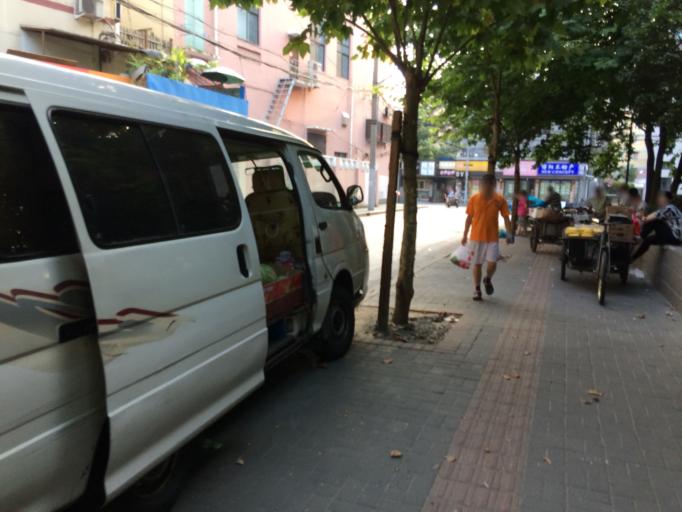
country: CN
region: Shanghai Shi
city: Changning
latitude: 31.2072
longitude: 121.4271
